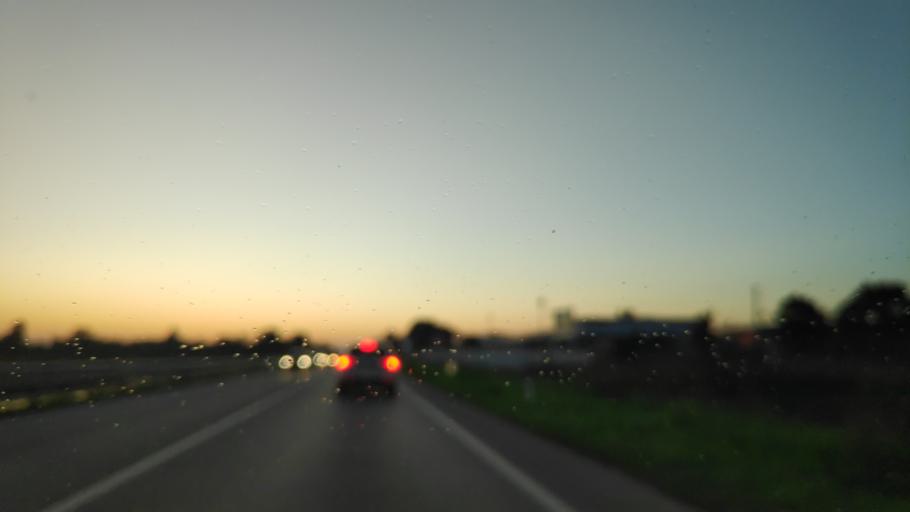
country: IT
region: Lombardy
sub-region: Citta metropolitana di Milano
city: Vermezzo
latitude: 45.4023
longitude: 8.9669
